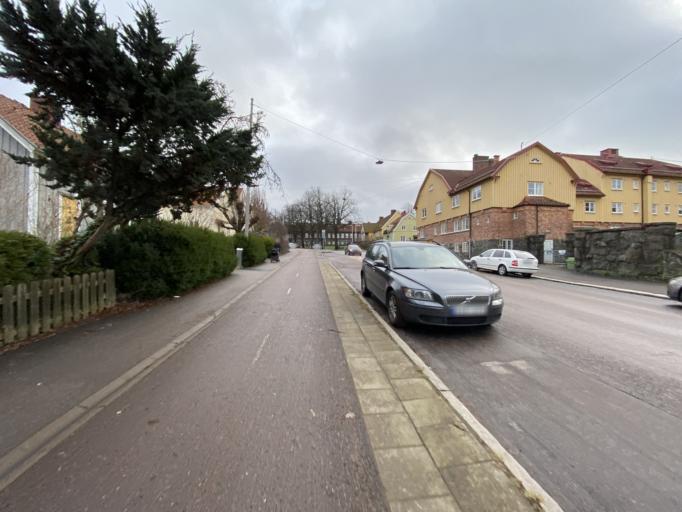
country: SE
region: Vaestra Goetaland
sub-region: Goteborg
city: Goeteborg
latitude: 57.7193
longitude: 12.0087
